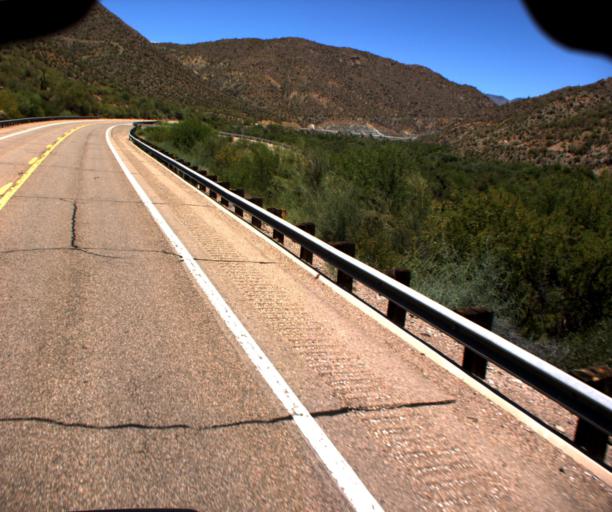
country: US
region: Arizona
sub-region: Pinal County
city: Kearny
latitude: 33.0594
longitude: -110.7218
